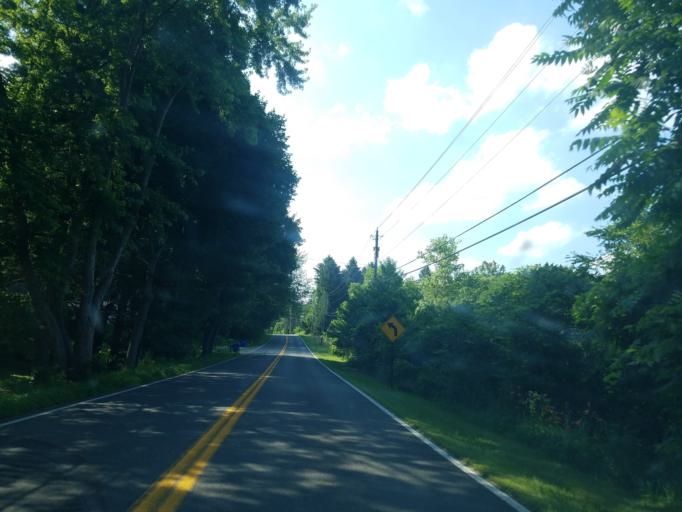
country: US
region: Ohio
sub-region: Summit County
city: Mogadore
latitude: 41.0487
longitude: -81.3664
